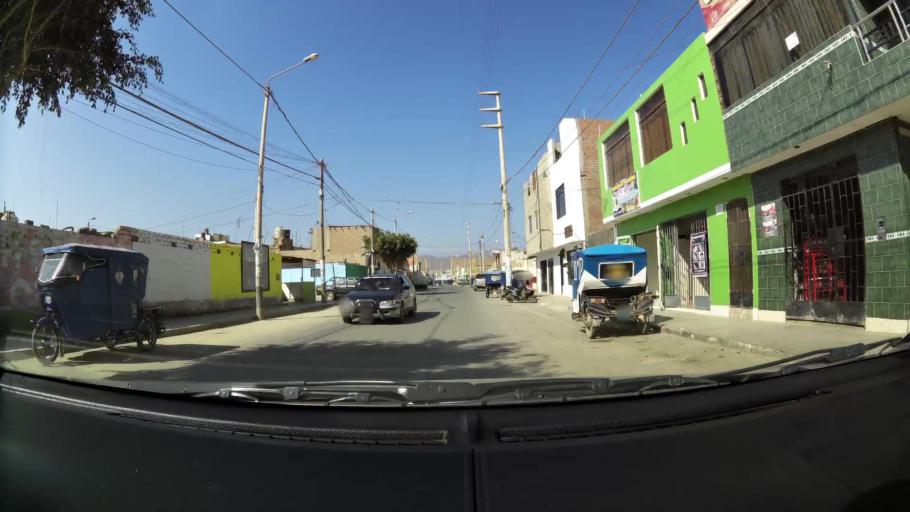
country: PE
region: Ancash
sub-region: Provincia de Huarmey
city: Huarmey
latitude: -10.0682
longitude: -78.1535
